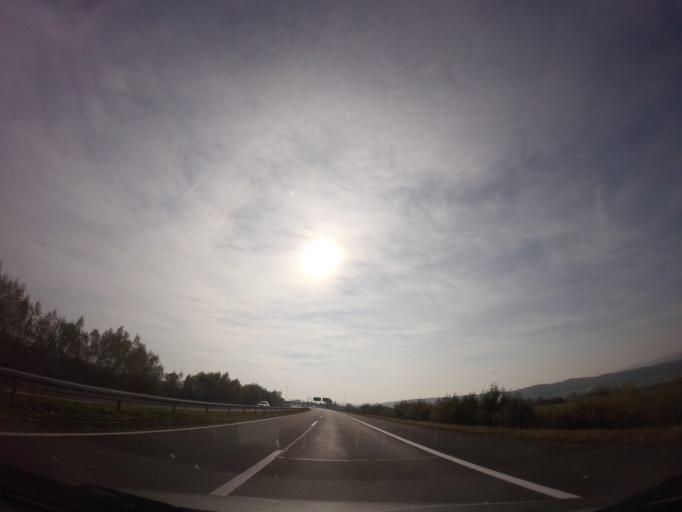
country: HR
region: Zagrebacka
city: Brckovljani
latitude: 45.9980
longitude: 16.2882
